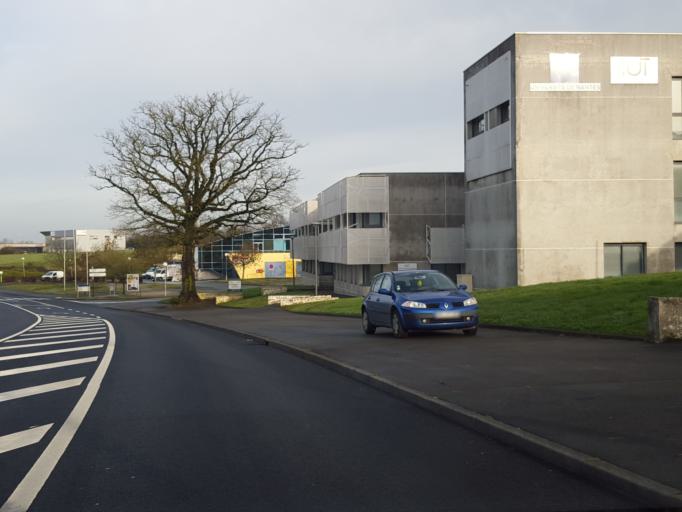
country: FR
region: Pays de la Loire
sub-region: Departement de la Vendee
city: La Roche-sur-Yon
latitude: 46.6766
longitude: -1.4053
